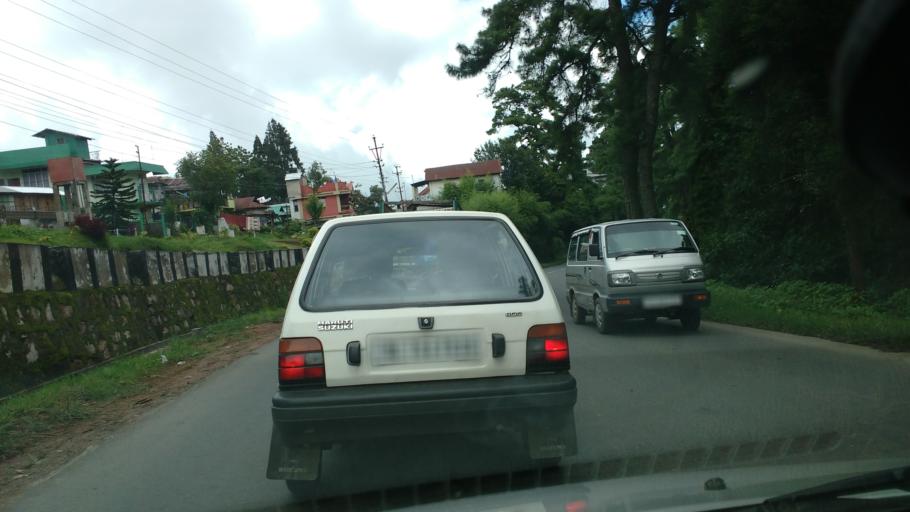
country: IN
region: Meghalaya
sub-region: East Khasi Hills
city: Shillong
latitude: 25.5600
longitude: 91.8503
